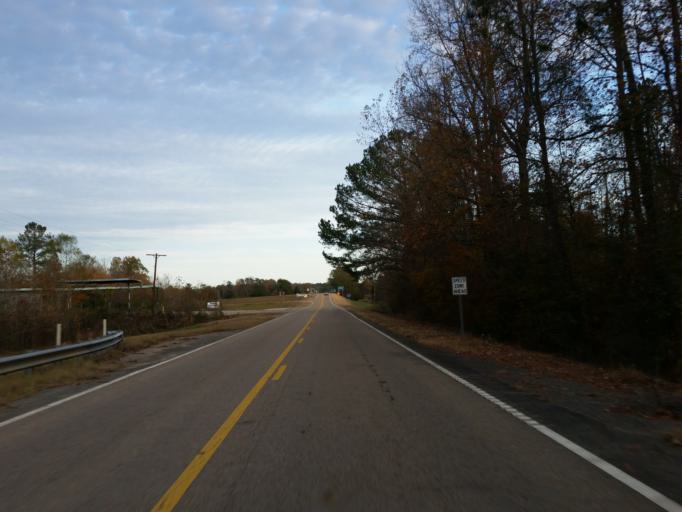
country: US
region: Alabama
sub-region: Sumter County
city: York
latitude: 32.4265
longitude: -88.4578
